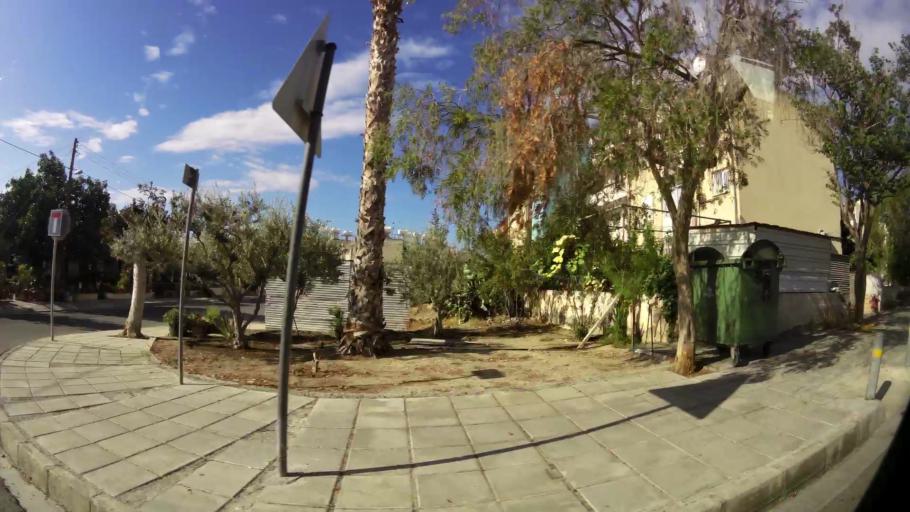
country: CY
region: Lefkosia
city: Nicosia
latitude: 35.1332
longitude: 33.3666
